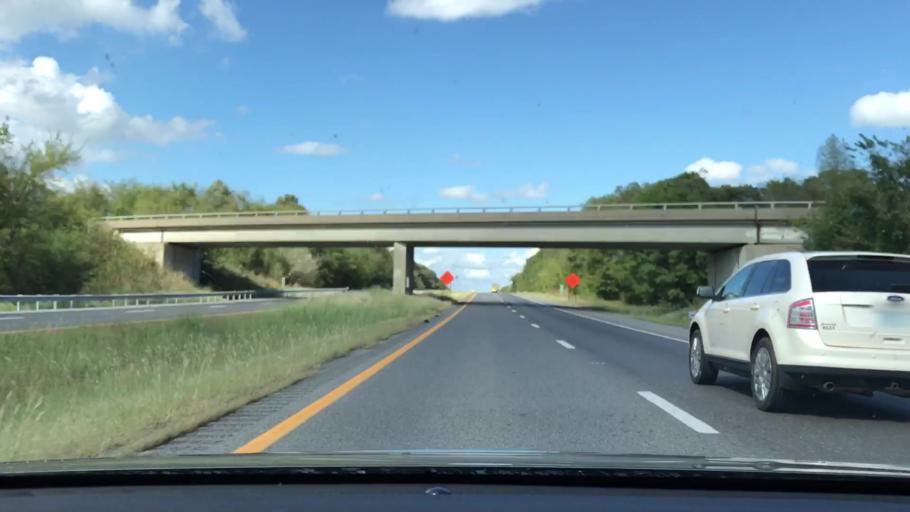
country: US
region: Kentucky
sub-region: Marshall County
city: Calvert City
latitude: 36.9552
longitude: -88.3496
